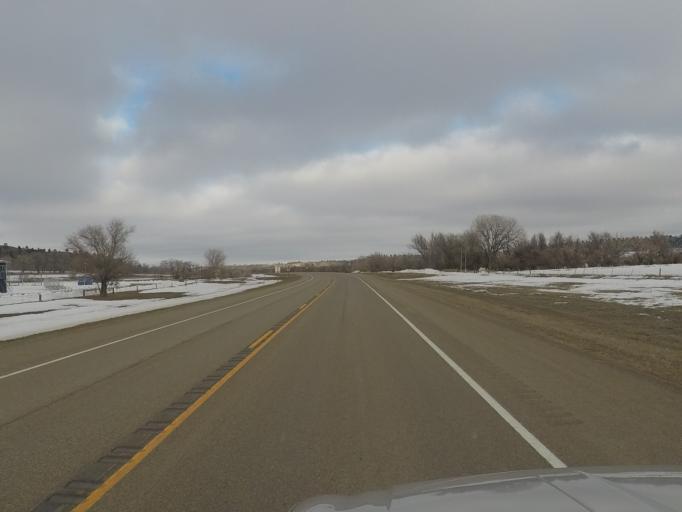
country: US
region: Montana
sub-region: Golden Valley County
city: Ryegate
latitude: 46.2968
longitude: -109.2444
